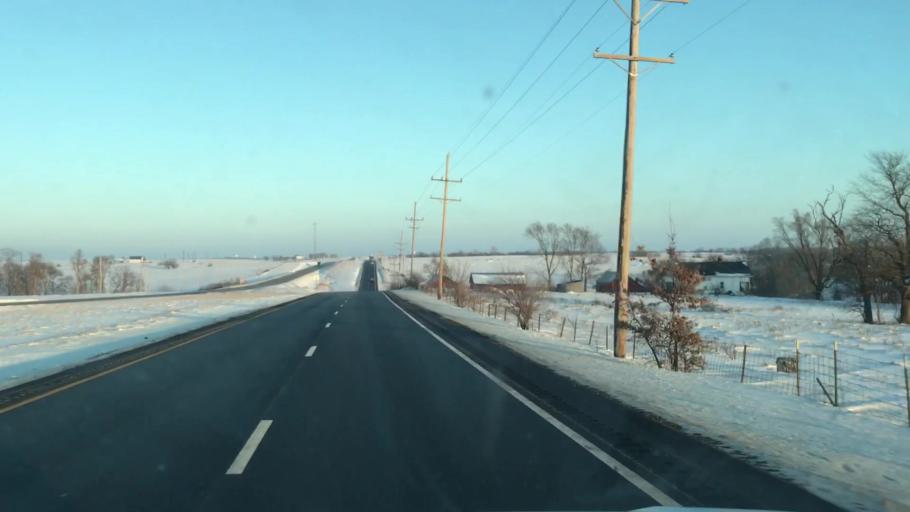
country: US
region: Missouri
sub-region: Clinton County
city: Cameron
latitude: 39.7545
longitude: -94.2997
